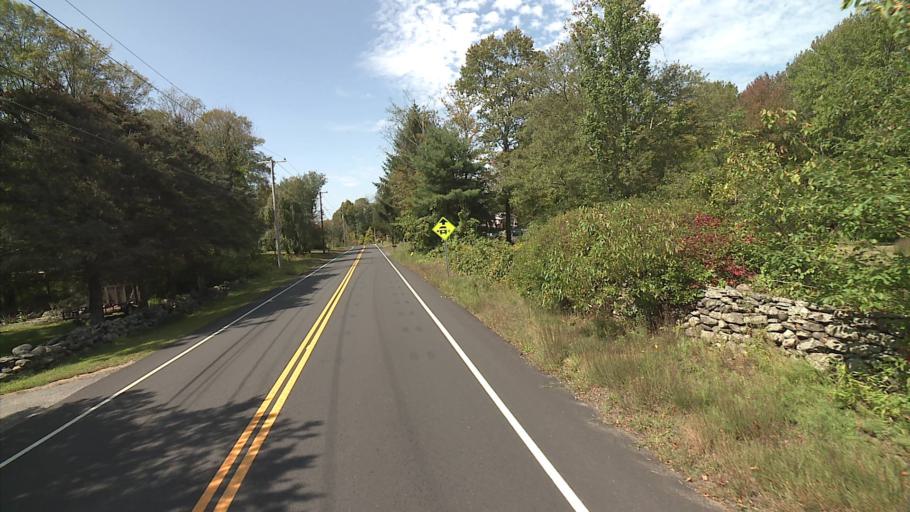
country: US
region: Connecticut
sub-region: Tolland County
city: Coventry Lake
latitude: 41.7214
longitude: -72.3407
